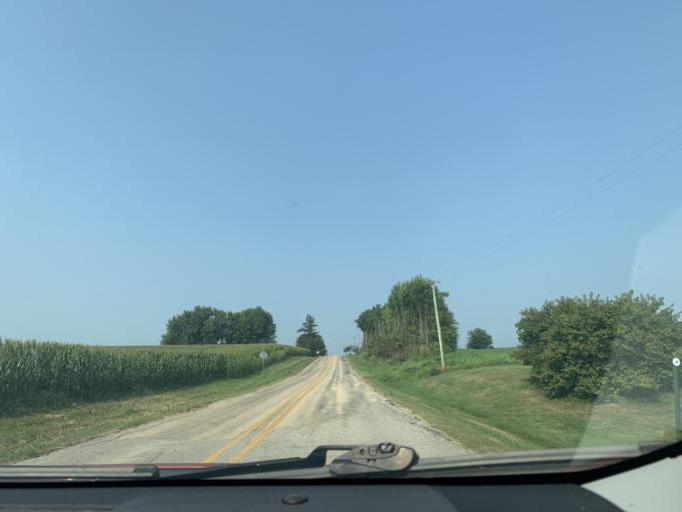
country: US
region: Illinois
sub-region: Carroll County
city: Milledgeville
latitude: 41.8479
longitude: -89.8060
